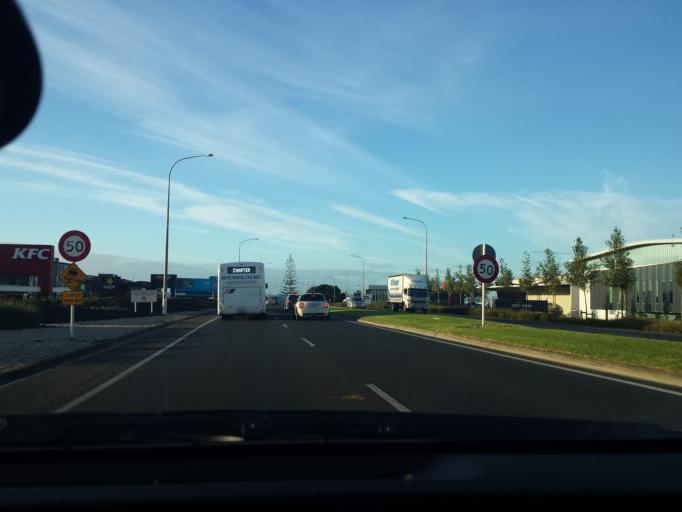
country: NZ
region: Auckland
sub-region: Auckland
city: Mangere
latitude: -36.9965
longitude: 174.7865
